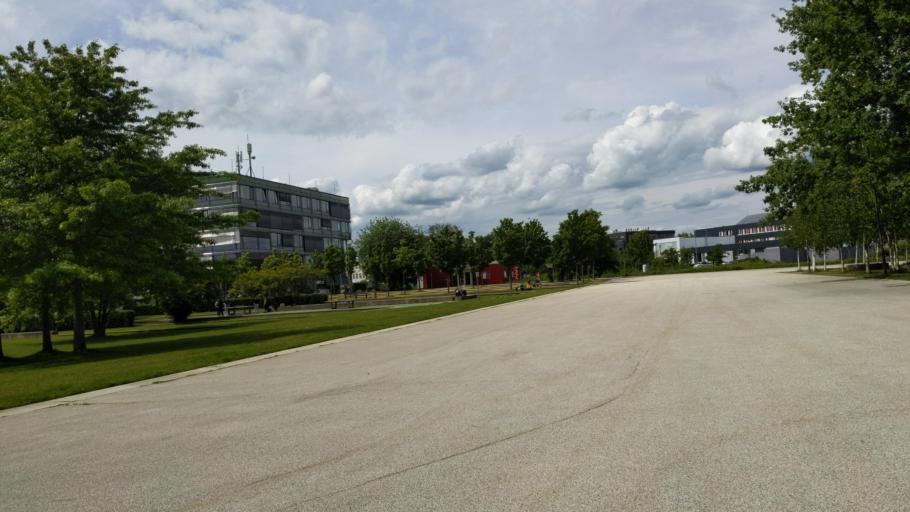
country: DE
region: Schleswig-Holstein
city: Luebeck
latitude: 53.8344
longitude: 10.6995
